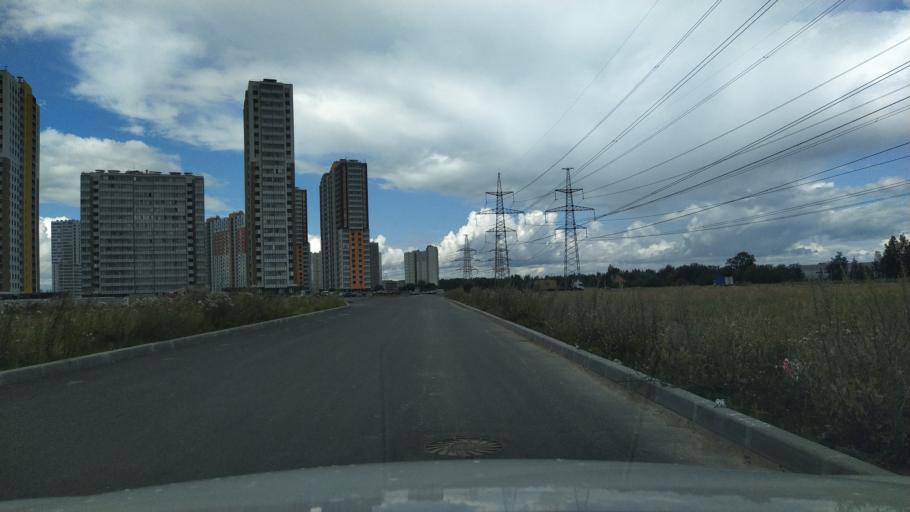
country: RU
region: St.-Petersburg
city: Krasnogvargeisky
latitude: 60.0052
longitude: 30.4834
